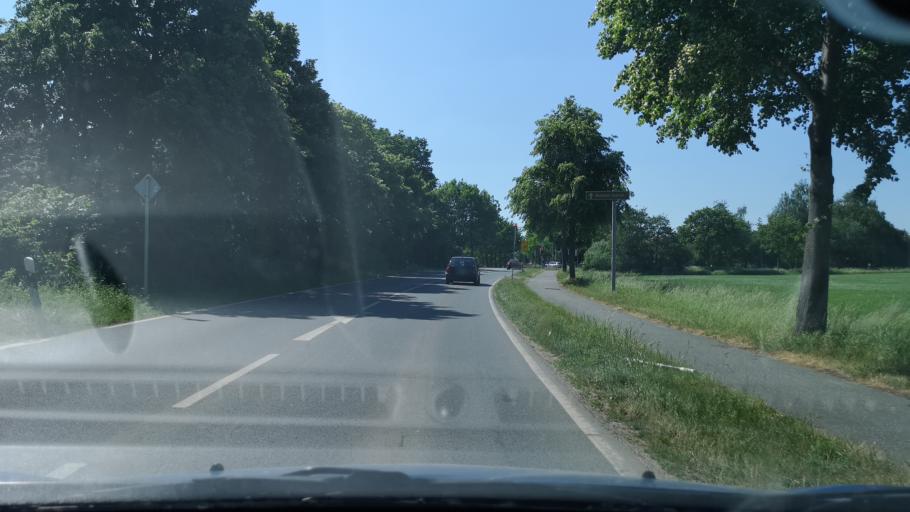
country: DE
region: Lower Saxony
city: Garbsen-Mitte
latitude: 52.4236
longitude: 9.6120
